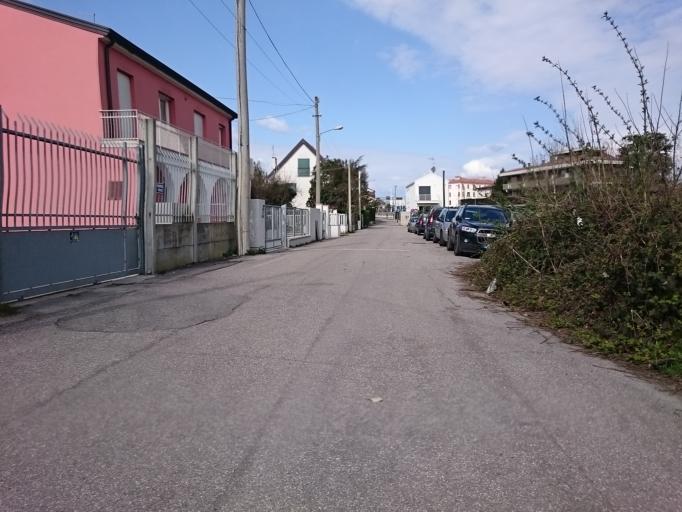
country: IT
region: Veneto
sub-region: Provincia di Padova
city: Mandriola-Sant'Agostino
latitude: 45.3834
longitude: 11.8632
